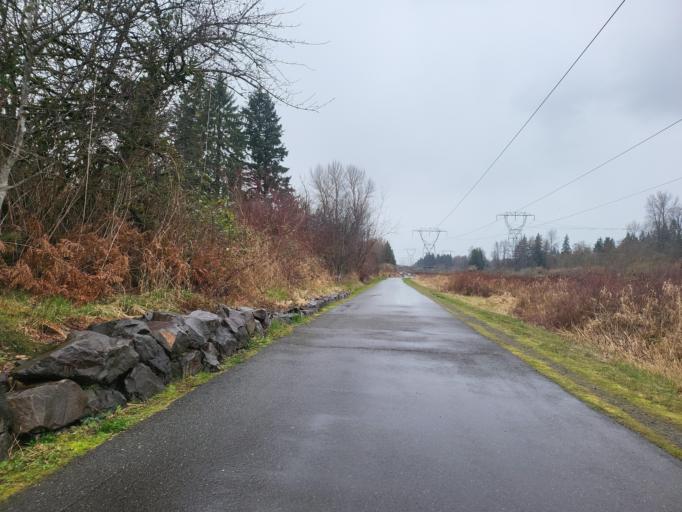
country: US
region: Washington
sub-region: King County
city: East Hill-Meridian
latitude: 47.4261
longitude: -122.1733
